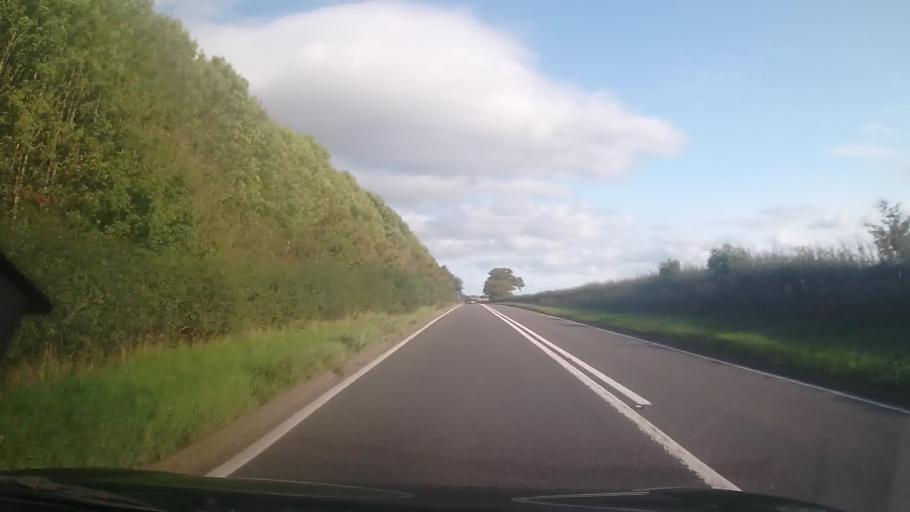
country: GB
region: England
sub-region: Shropshire
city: Bromfield
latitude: 52.3968
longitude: -2.7915
